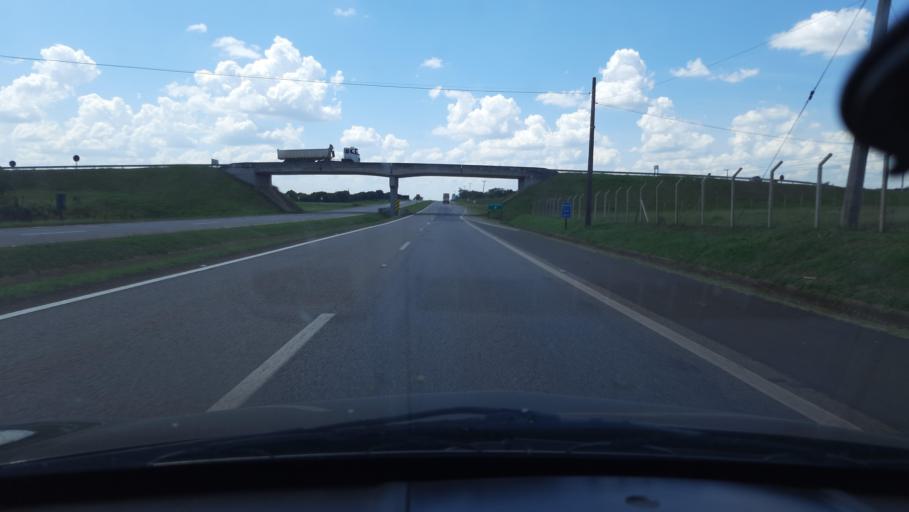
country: BR
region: Sao Paulo
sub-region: Casa Branca
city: Casa Branca
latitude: -21.7499
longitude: -47.0715
